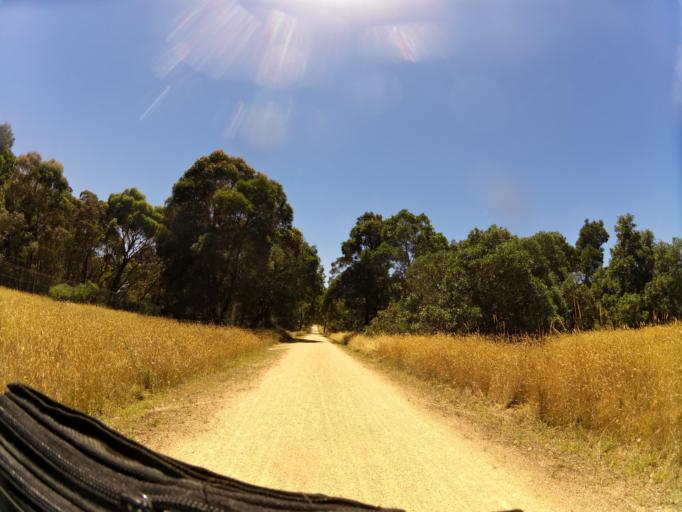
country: AU
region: Victoria
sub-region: Ballarat North
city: Delacombe
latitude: -37.6317
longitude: 143.6958
